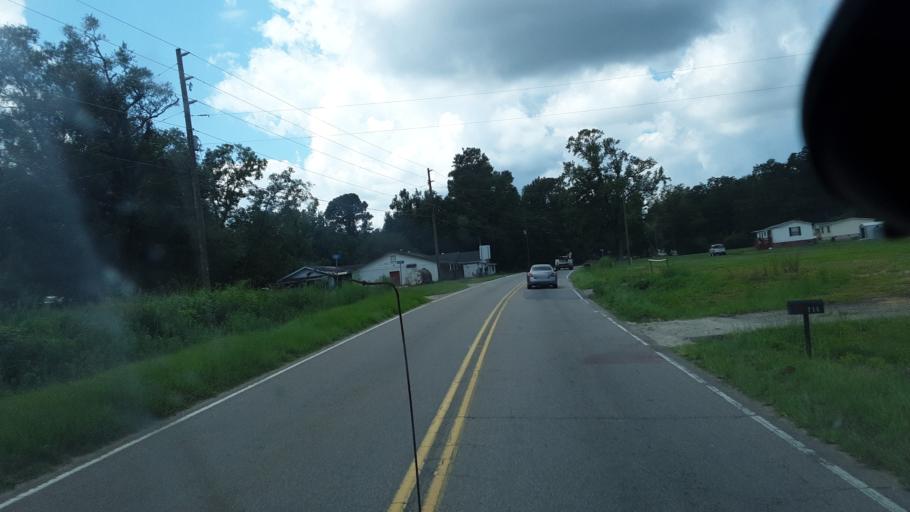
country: US
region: South Carolina
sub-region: Williamsburg County
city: Andrews
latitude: 33.3677
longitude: -79.4524
